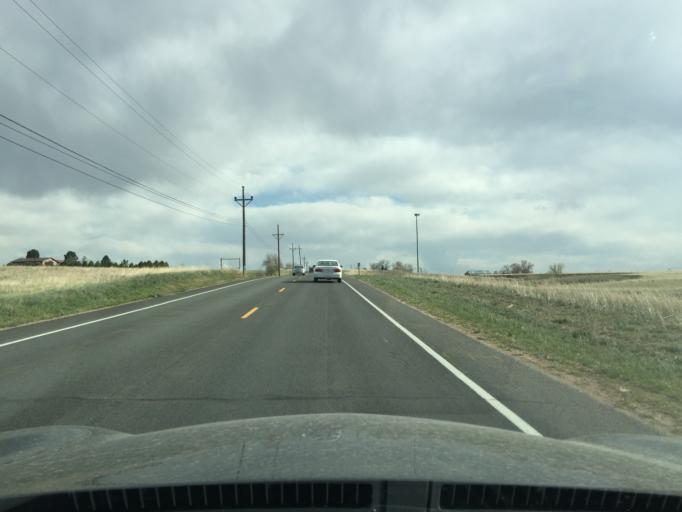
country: US
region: Colorado
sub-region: Boulder County
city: Niwot
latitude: 40.0978
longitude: -105.1315
